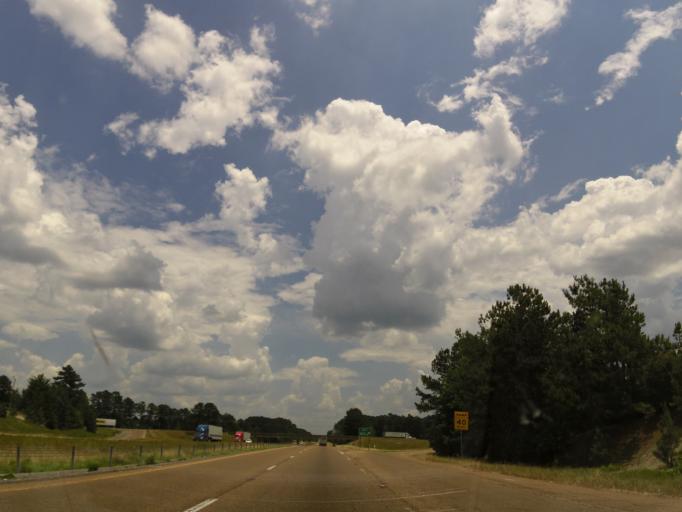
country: US
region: Mississippi
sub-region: Lauderdale County
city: Marion
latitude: 32.3946
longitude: -88.5831
